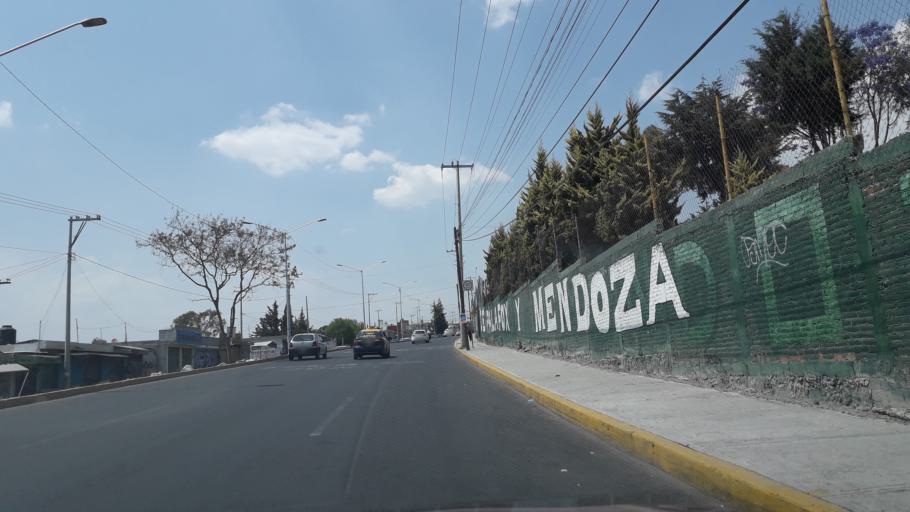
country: MX
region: Puebla
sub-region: Puebla
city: Galaxia la Calera
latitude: 18.9956
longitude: -98.1796
